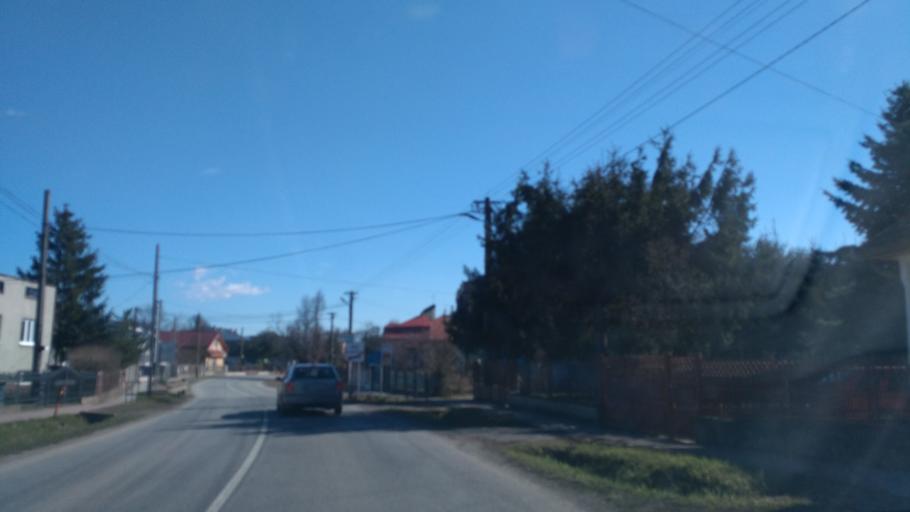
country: SK
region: Kosicky
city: Kosice
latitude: 48.6293
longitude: 21.3050
